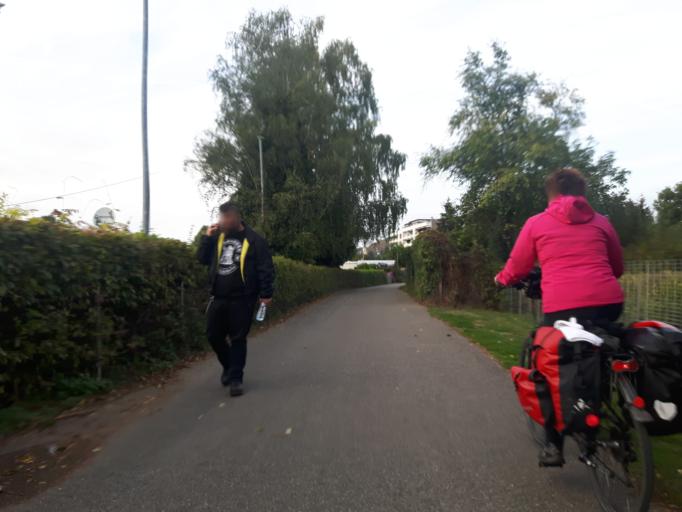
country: DE
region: Rheinland-Pfalz
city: Bad Honningen
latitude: 50.5091
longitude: 7.3111
